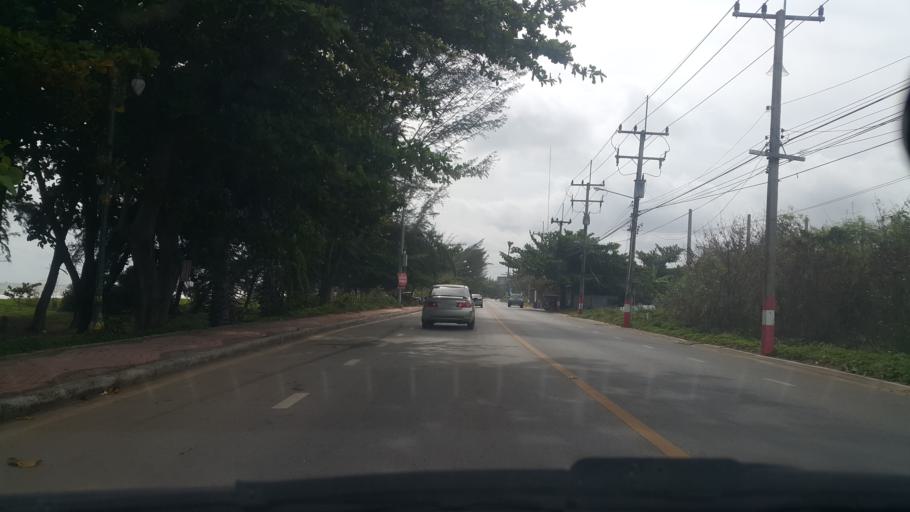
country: TH
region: Rayong
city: Rayong
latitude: 12.6312
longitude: 101.3444
